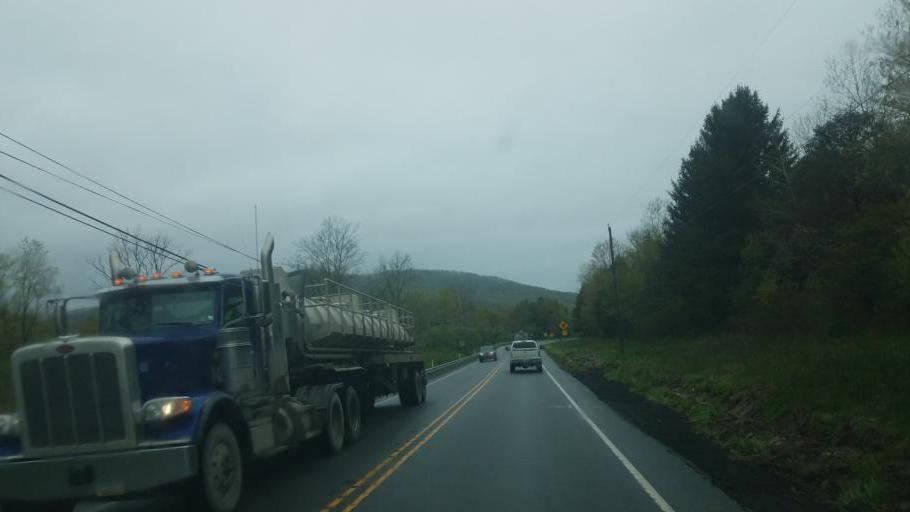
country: US
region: Pennsylvania
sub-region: McKean County
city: Smethport
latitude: 41.8097
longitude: -78.4158
